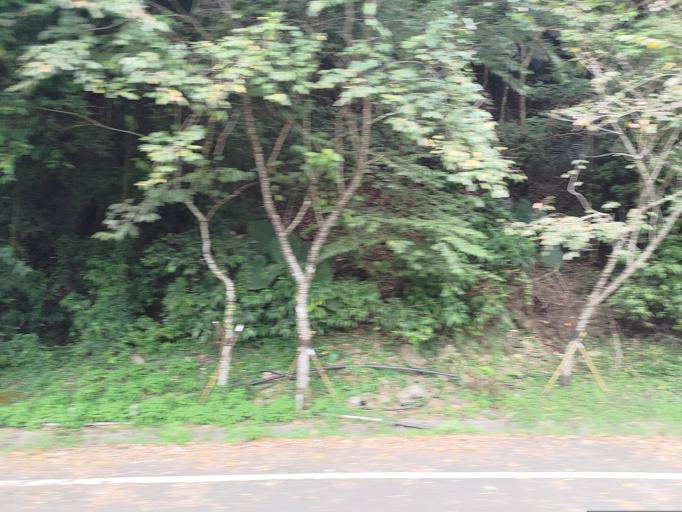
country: TW
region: Taiwan
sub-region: Miaoli
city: Miaoli
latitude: 24.5989
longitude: 121.0237
